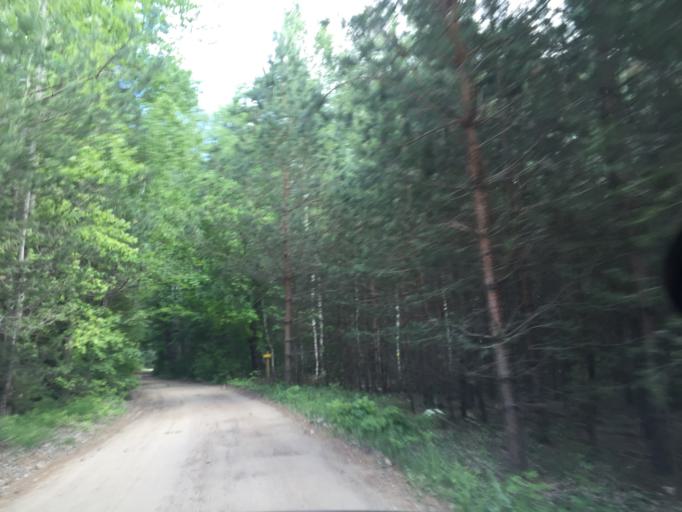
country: LV
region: Vecumnieki
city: Vecumnieki
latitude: 56.4239
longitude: 24.5188
